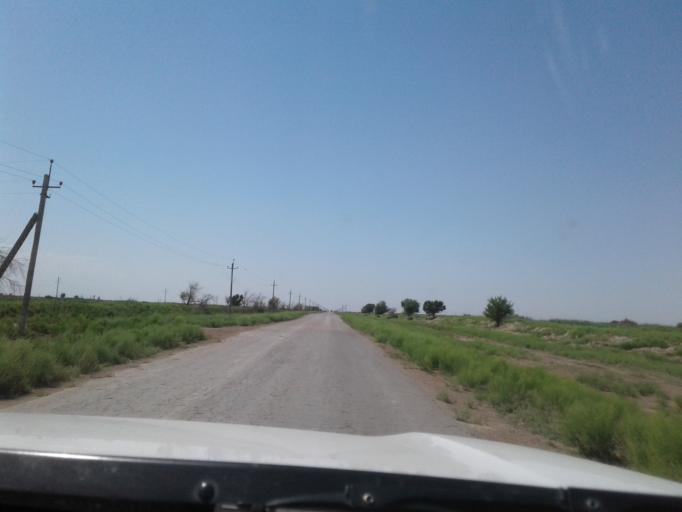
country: TM
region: Dasoguz
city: Koeneuergench
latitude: 41.8498
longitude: 58.7049
